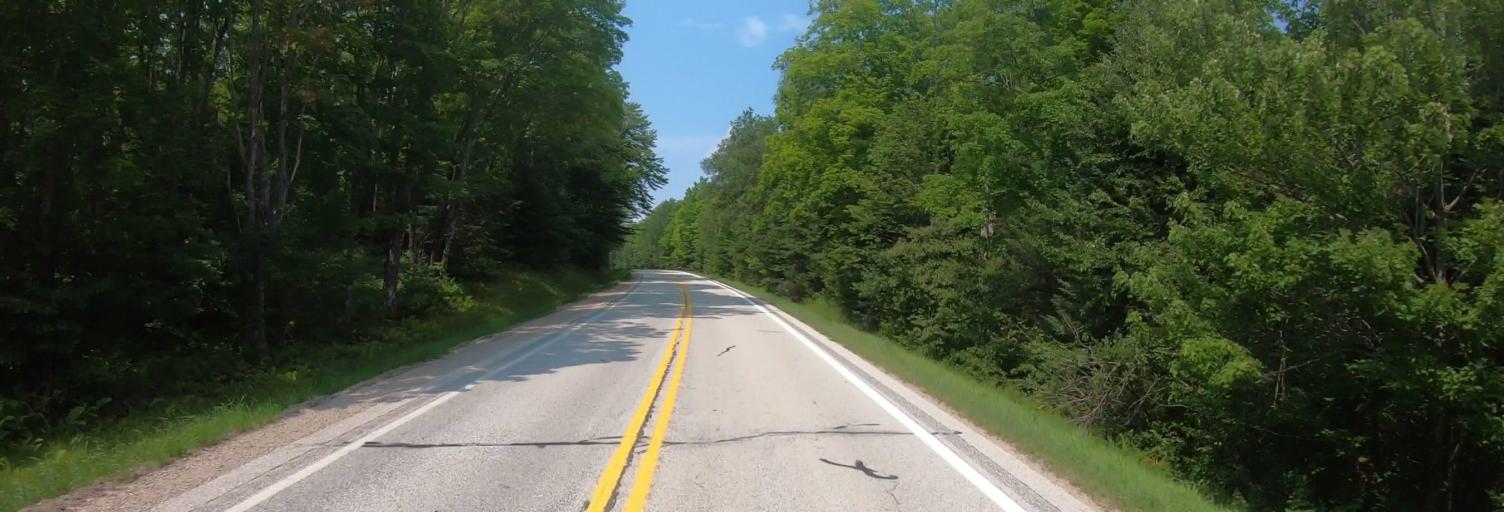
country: US
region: Michigan
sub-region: Luce County
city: Newberry
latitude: 46.5637
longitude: -85.3493
